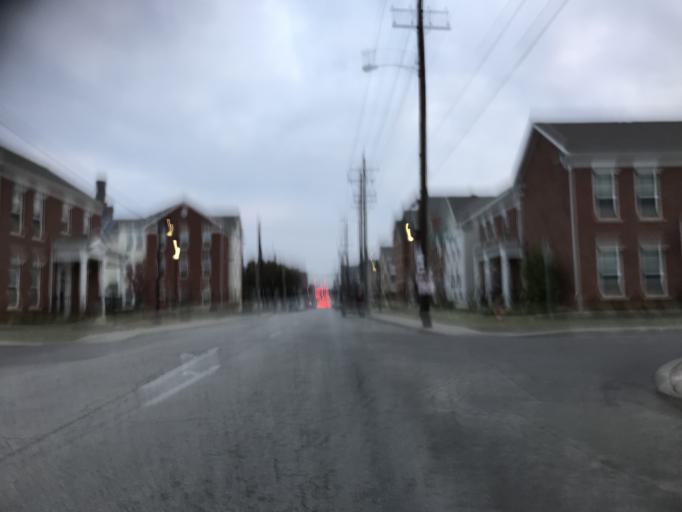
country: US
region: Kentucky
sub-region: Jefferson County
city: Louisville
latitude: 38.2426
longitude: -85.7460
